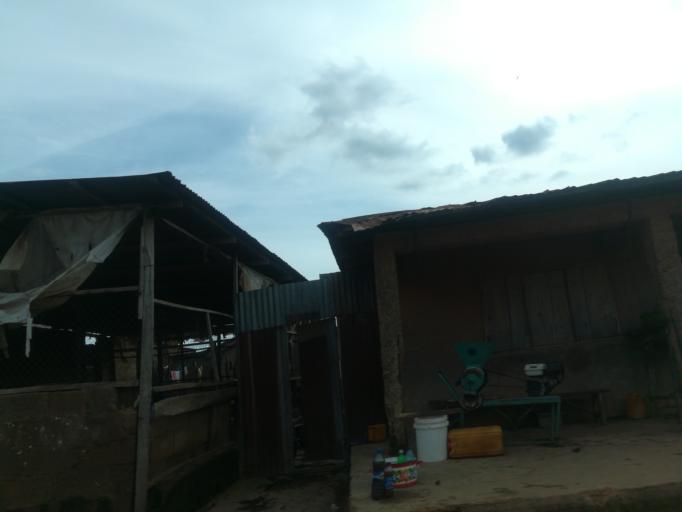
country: NG
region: Oyo
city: Ibadan
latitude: 7.3817
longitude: 3.9440
